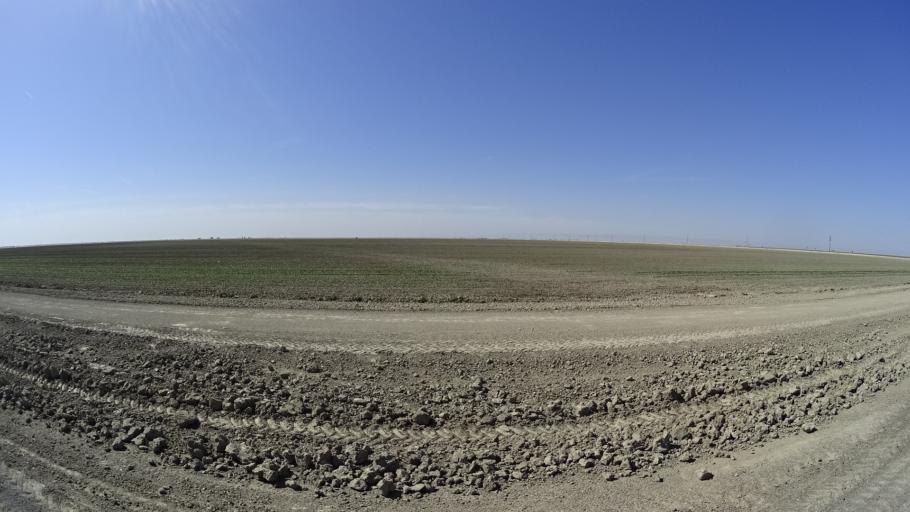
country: US
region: California
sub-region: Tulare County
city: Alpaugh
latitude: 35.8912
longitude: -119.5706
